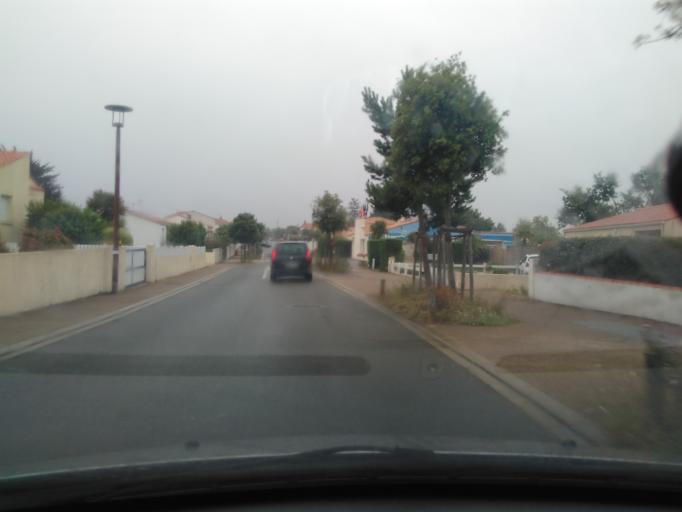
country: FR
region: Pays de la Loire
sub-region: Departement de la Vendee
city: Bretignolles-sur-Mer
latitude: 46.6306
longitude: -1.8596
